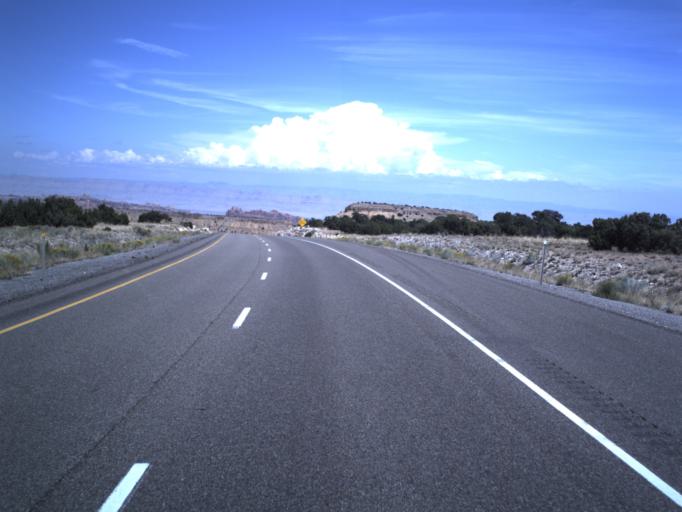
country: US
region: Utah
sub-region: Emery County
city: Castle Dale
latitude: 38.9059
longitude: -110.5323
